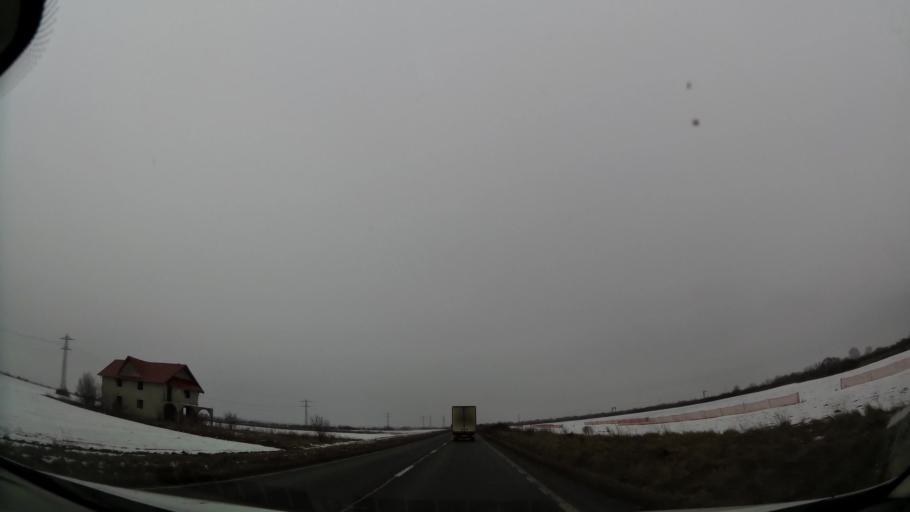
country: RO
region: Dambovita
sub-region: Comuna Racari
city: Mavrodin
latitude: 44.6421
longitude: 25.7064
